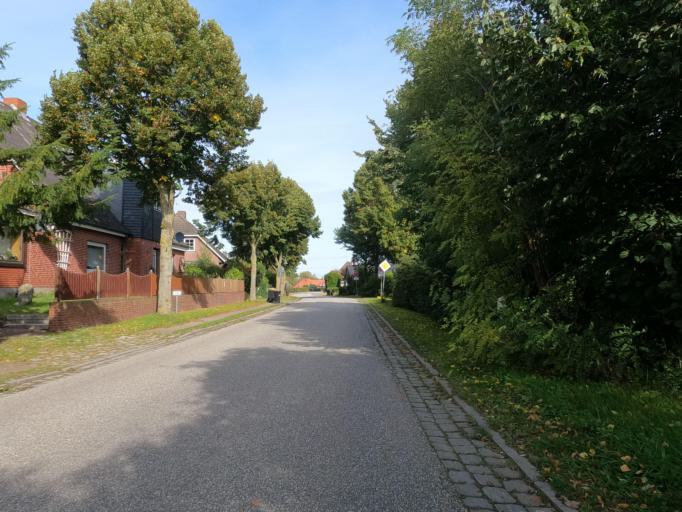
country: DE
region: Schleswig-Holstein
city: Riepsdorf
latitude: 54.2226
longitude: 10.9675
